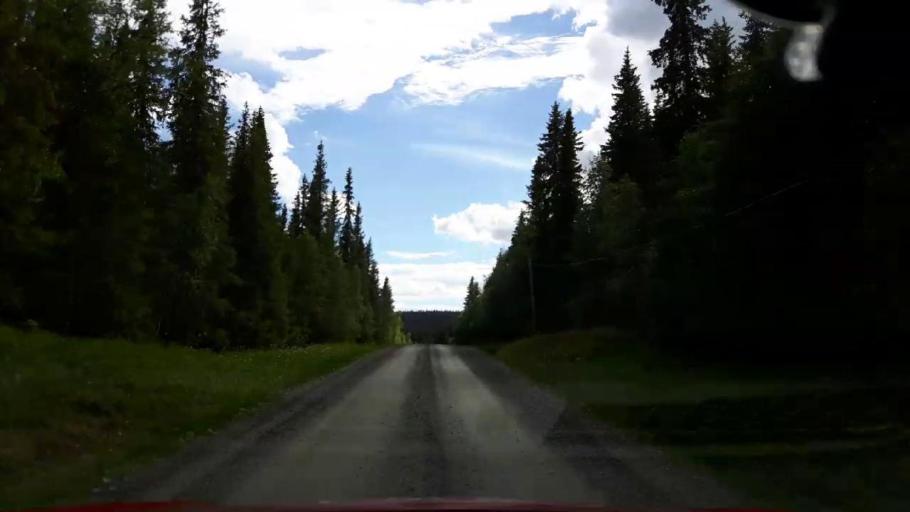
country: SE
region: Jaemtland
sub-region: Krokoms Kommun
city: Valla
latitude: 63.8379
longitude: 14.0445
